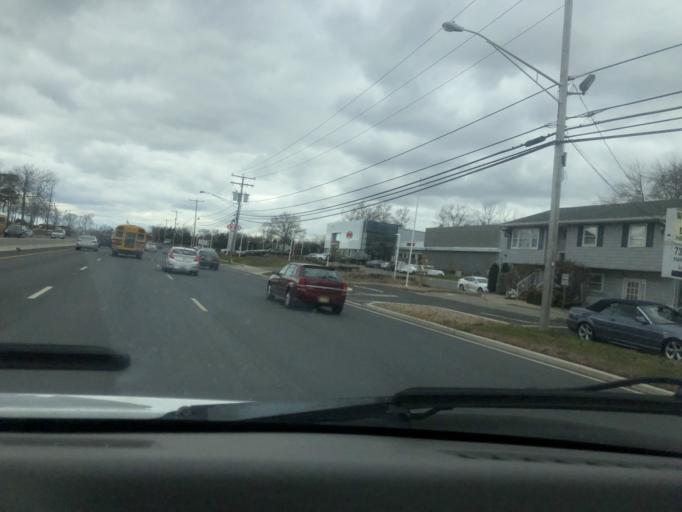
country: US
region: New Jersey
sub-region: Ocean County
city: Holiday City South
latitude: 39.9750
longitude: -74.2423
